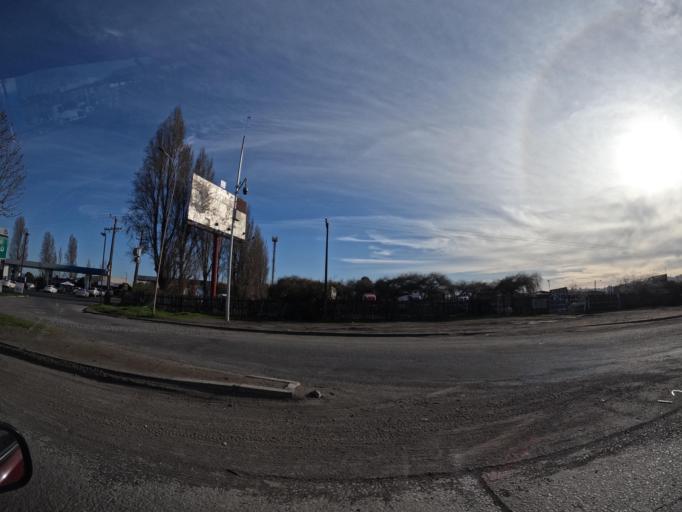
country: CL
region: Biobio
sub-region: Provincia de Concepcion
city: Concepcion
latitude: -36.7789
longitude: -73.0782
